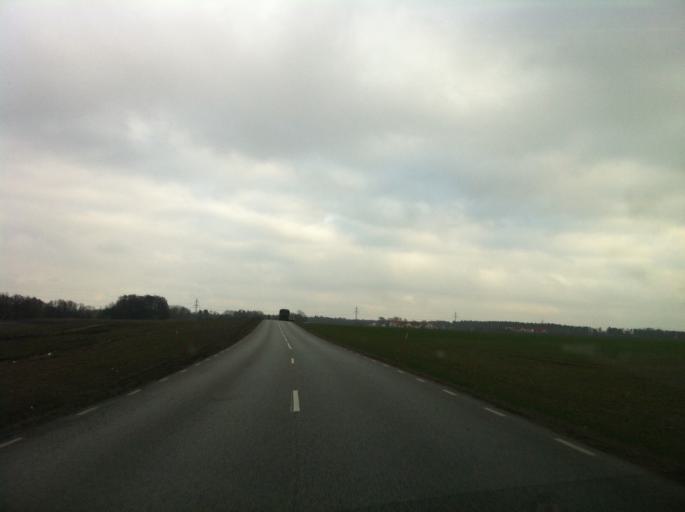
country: SE
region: Skane
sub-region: Kavlinge Kommun
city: Hofterup
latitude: 55.8261
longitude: 12.9795
